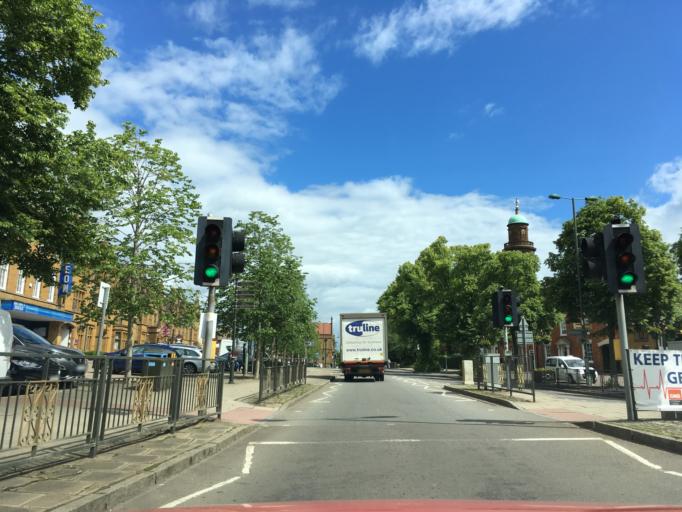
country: GB
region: England
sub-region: Oxfordshire
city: Banbury
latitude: 52.0604
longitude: -1.3403
